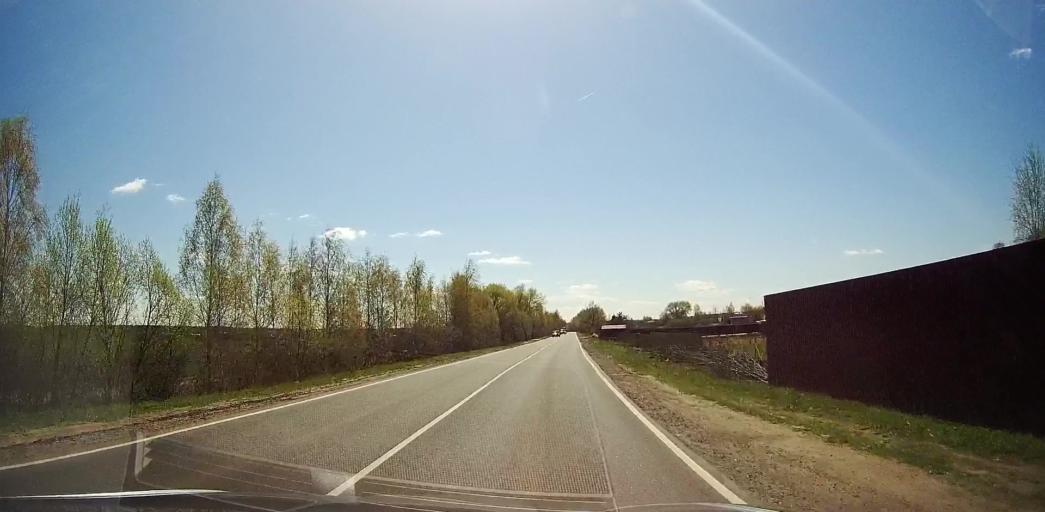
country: RU
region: Moskovskaya
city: Beloozerskiy
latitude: 55.5207
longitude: 38.4350
